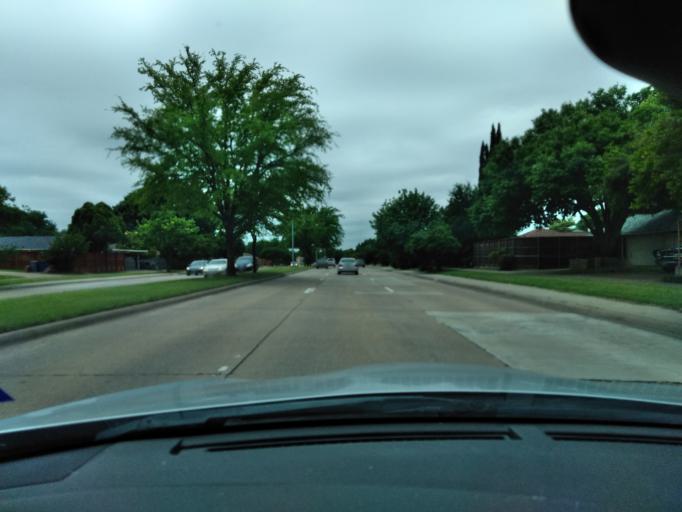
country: US
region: Texas
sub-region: Dallas County
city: Addison
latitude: 32.9701
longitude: -96.7847
